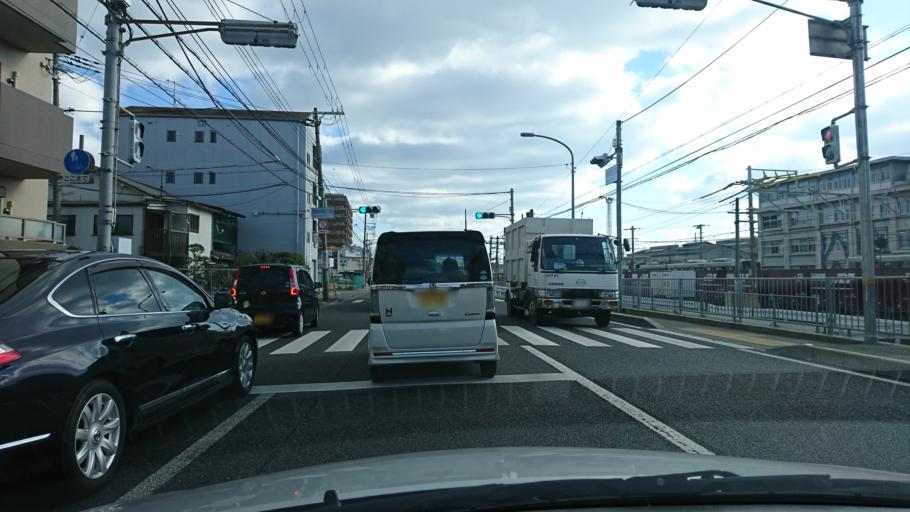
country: JP
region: Hyogo
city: Akashi
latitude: 34.6628
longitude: 134.9663
